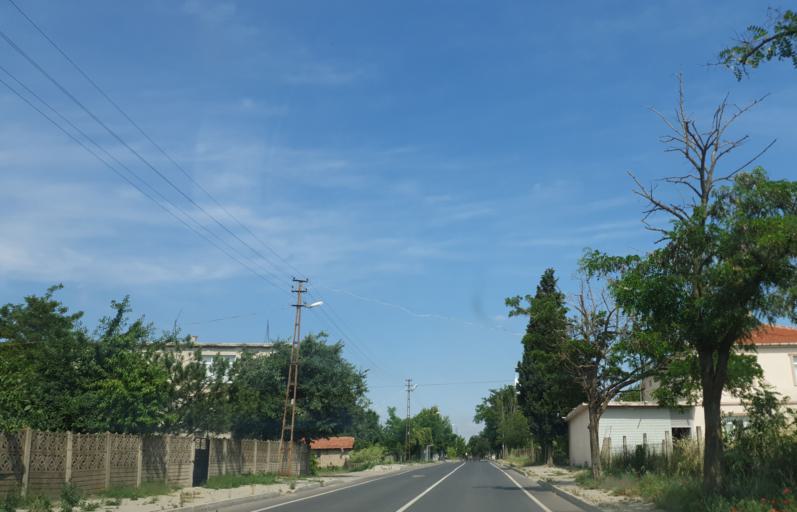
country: TR
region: Kirklareli
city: Buyukkaristiran
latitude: 41.2611
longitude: 27.6403
